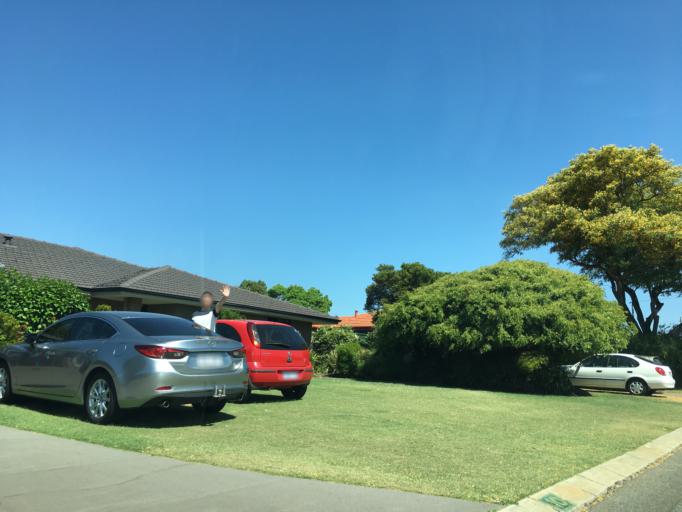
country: AU
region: Western Australia
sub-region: Canning
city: Willetton
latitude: -32.0464
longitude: 115.8997
